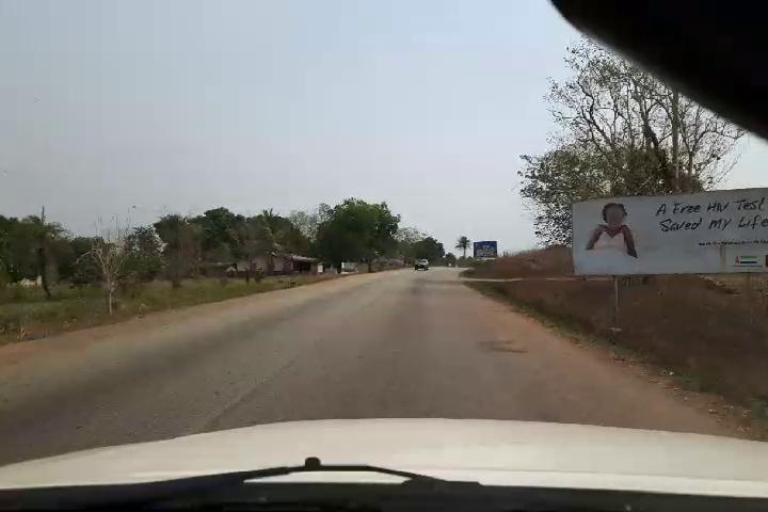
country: SL
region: Southern Province
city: Largo
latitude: 8.3169
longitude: -12.2174
